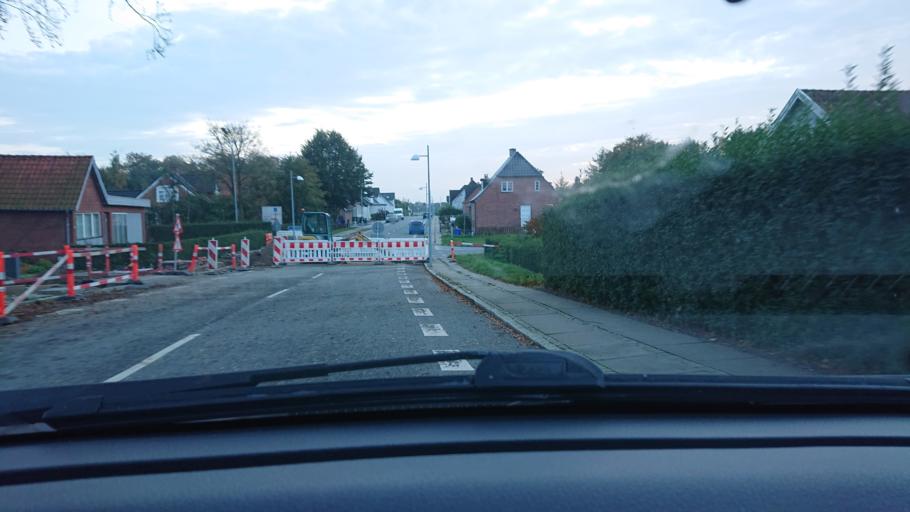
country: DK
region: South Denmark
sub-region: Nyborg Kommune
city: Ullerslev
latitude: 55.3569
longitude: 10.6702
